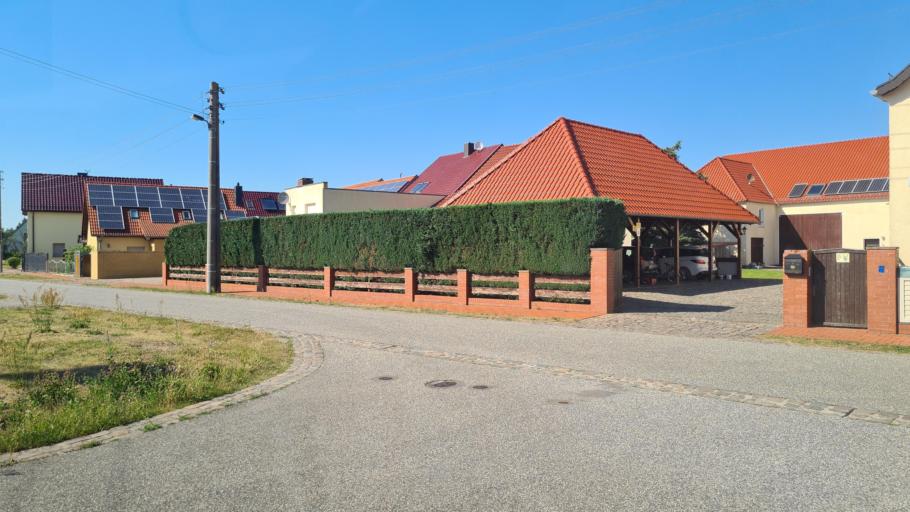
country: DE
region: Saxony-Anhalt
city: Annaburg
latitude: 51.6986
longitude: 12.9932
